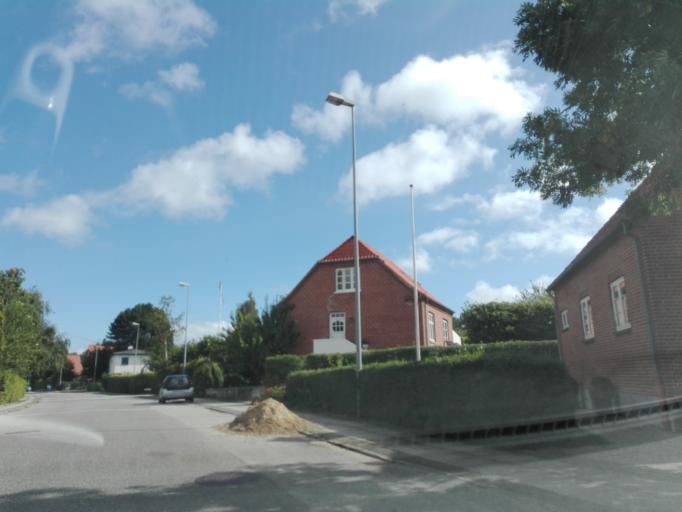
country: DK
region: Central Jutland
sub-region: Arhus Kommune
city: Arhus
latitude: 56.1122
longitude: 10.2025
